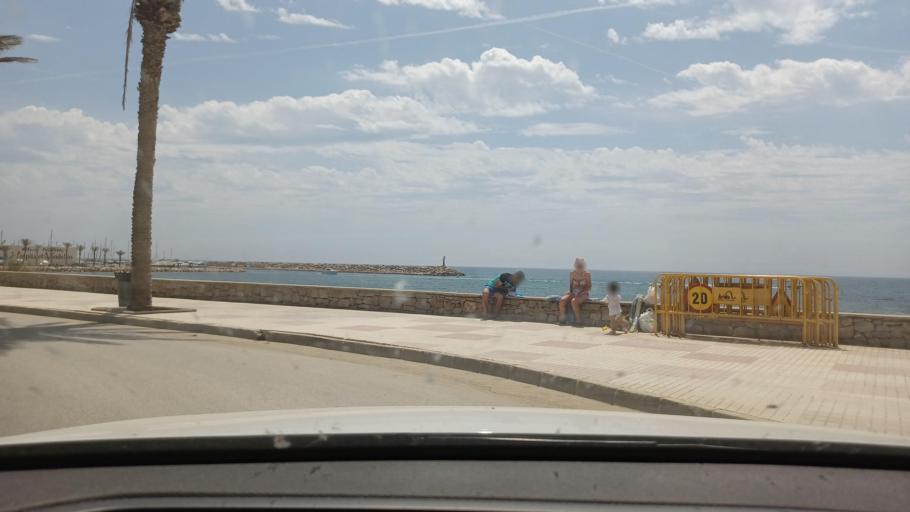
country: ES
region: Catalonia
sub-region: Provincia de Tarragona
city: Colldejou
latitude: 40.9884
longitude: 0.9236
